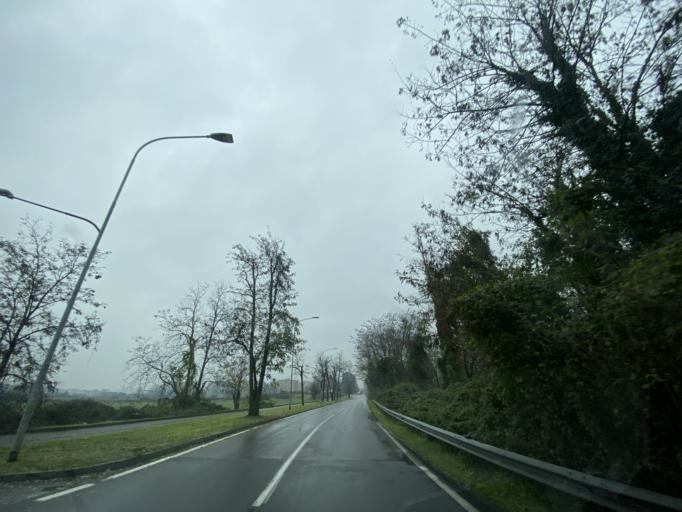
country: IT
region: Lombardy
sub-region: Citta metropolitana di Milano
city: Baranzate
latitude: 45.5359
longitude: 9.1149
